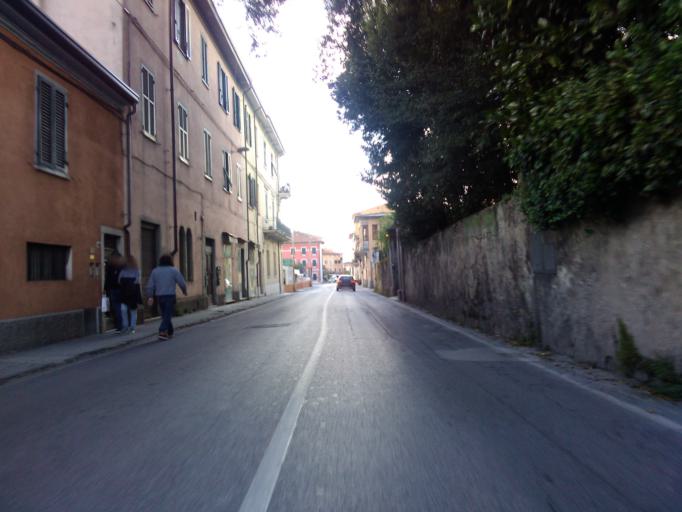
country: IT
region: Tuscany
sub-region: Provincia di Lucca
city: Pietrasanta
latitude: 43.9552
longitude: 10.2322
